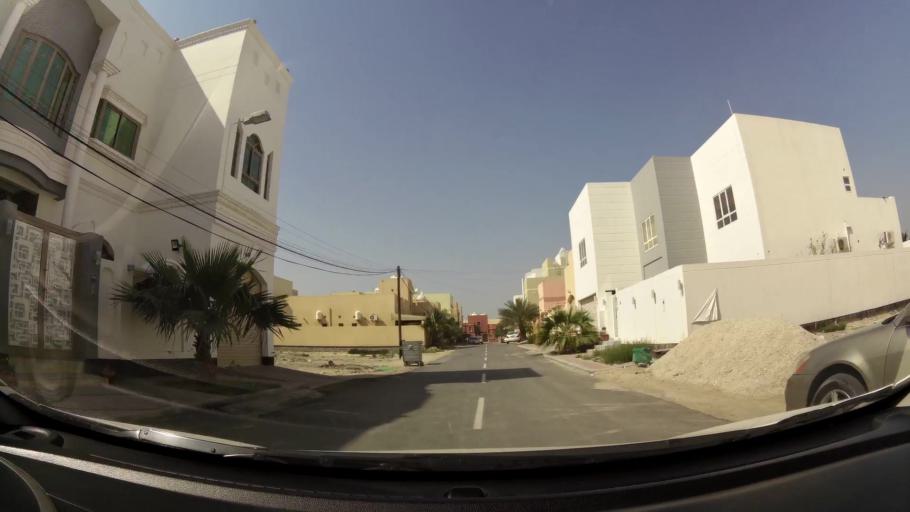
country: BH
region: Manama
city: Jidd Hafs
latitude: 26.2077
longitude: 50.4669
